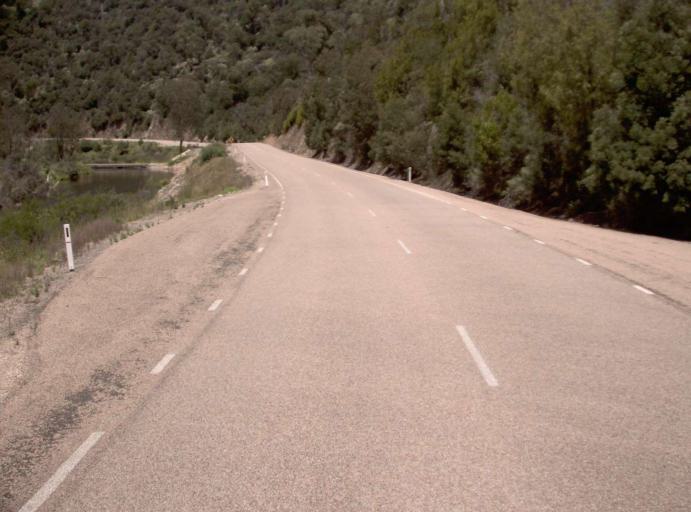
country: AU
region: Victoria
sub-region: East Gippsland
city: Lakes Entrance
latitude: -37.5494
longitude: 147.8670
